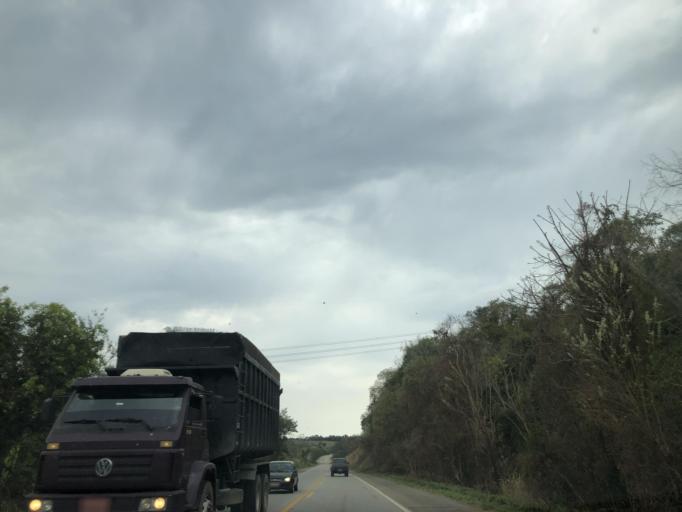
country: BR
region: Sao Paulo
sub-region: Salto De Pirapora
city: Salto de Pirapora
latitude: -23.7201
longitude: -47.6384
